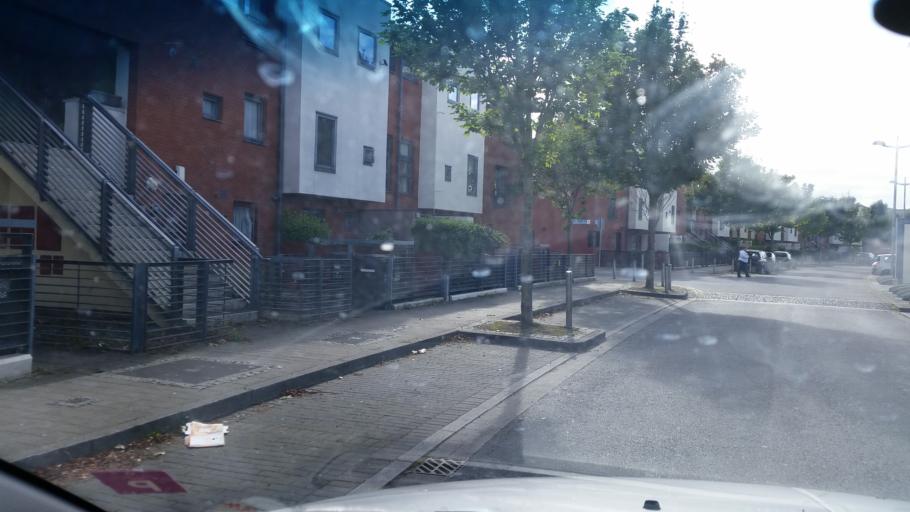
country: IE
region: Leinster
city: Ballymun
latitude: 53.3972
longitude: -6.2580
